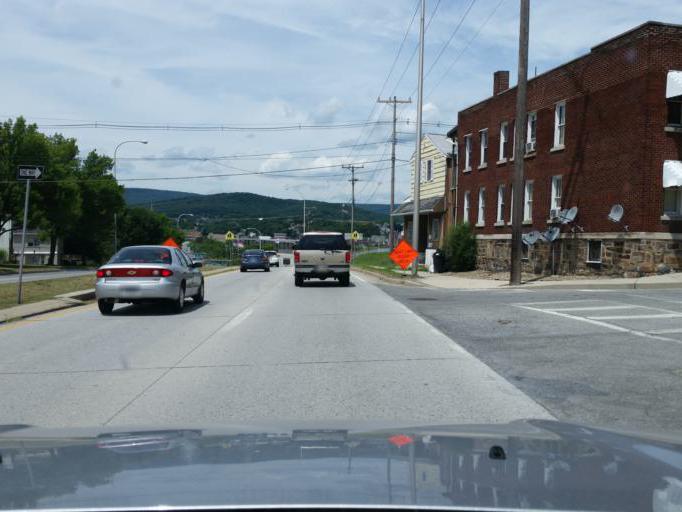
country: US
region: Pennsylvania
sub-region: Blair County
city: Altoona
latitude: 40.5055
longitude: -78.3969
